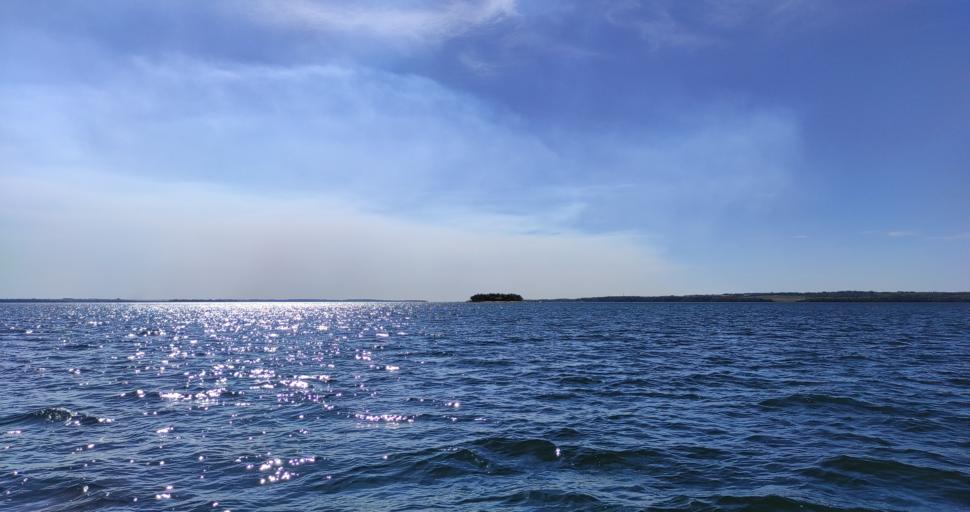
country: AR
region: Misiones
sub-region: Departamento de Capital
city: Posadas
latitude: -27.3437
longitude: -55.9402
